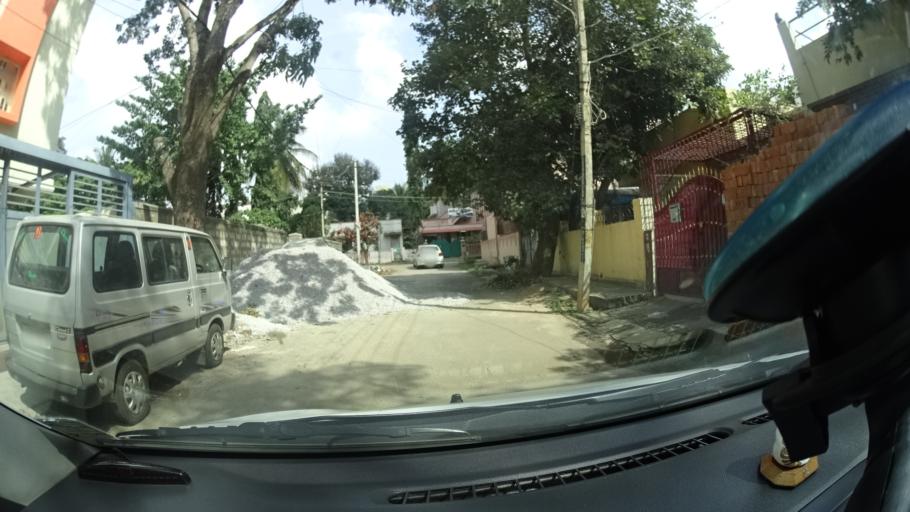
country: IN
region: Karnataka
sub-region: Bangalore Urban
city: Yelahanka
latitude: 13.0952
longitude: 77.5840
